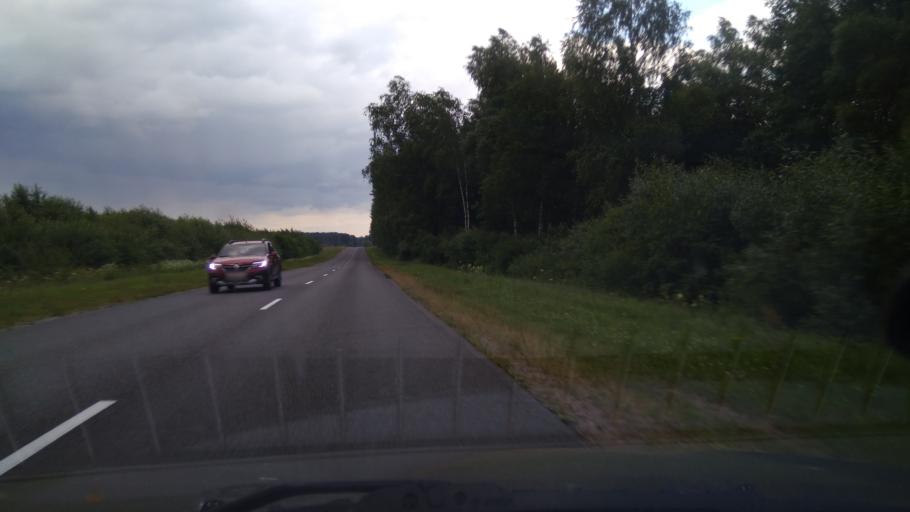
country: BY
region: Minsk
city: Il'ya
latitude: 54.4285
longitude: 27.1979
